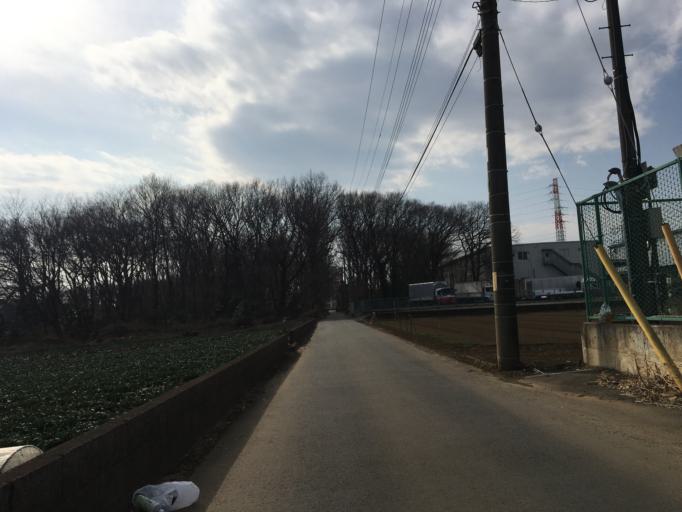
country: JP
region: Saitama
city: Oi
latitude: 35.8310
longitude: 139.5265
